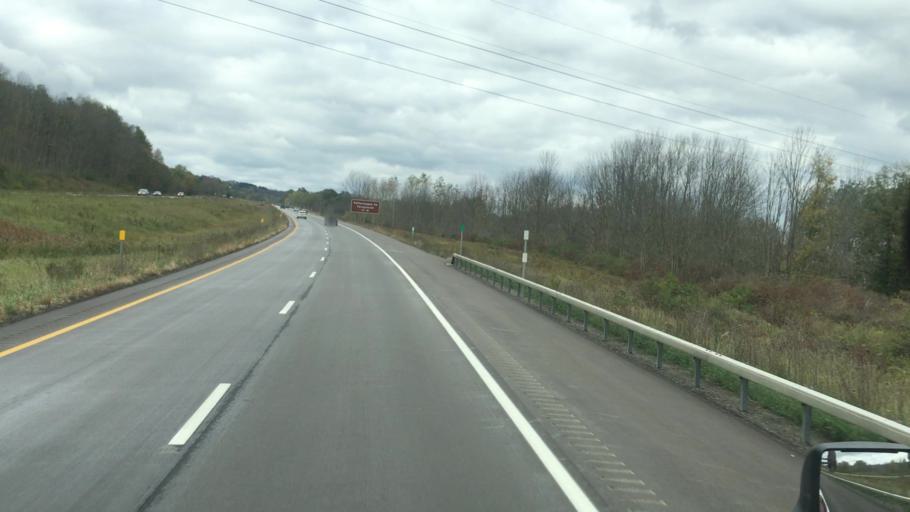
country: US
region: New York
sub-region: Cattaraugus County
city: Randolph
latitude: 42.1506
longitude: -78.9715
